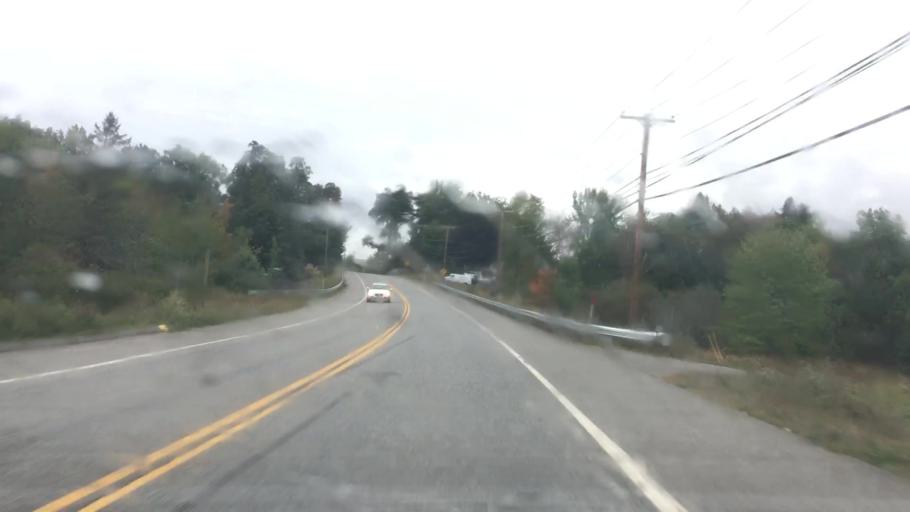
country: US
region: Maine
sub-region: Penobscot County
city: Orrington
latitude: 44.7251
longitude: -68.8270
